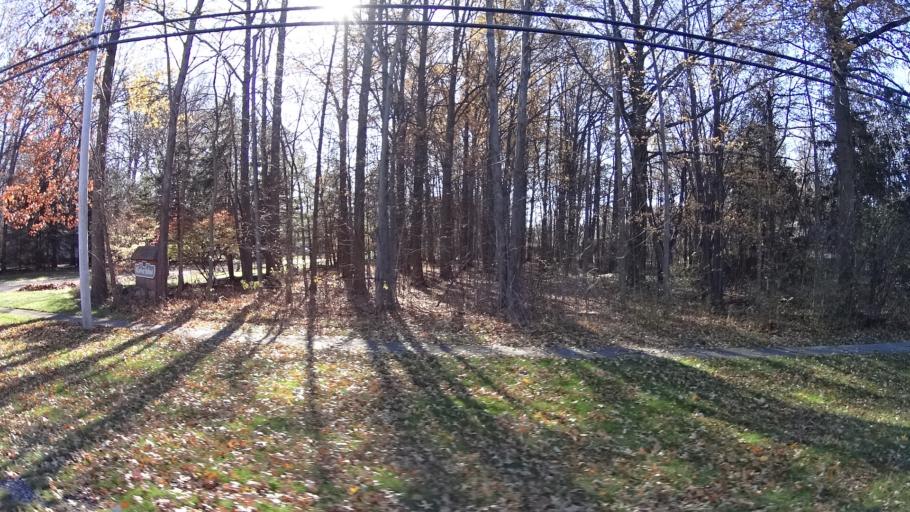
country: US
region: Ohio
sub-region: Lorain County
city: Avon Lake
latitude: 41.4931
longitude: -82.0100
